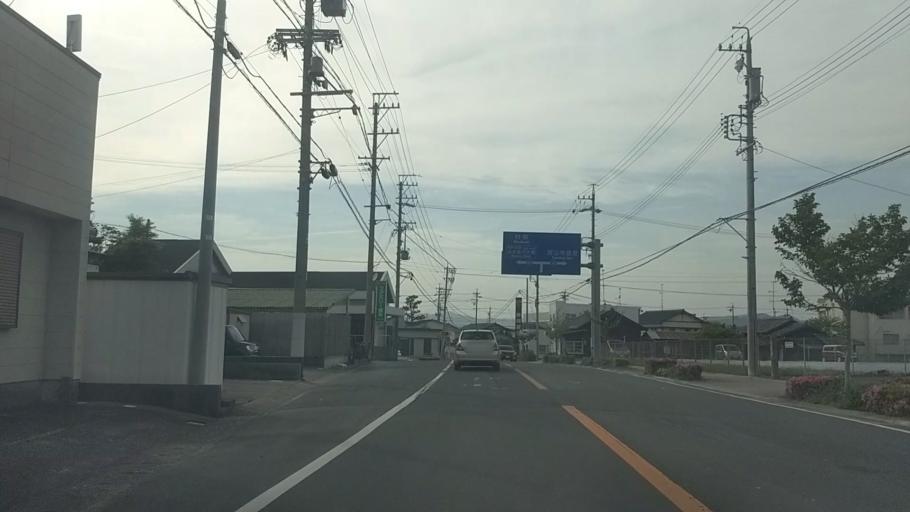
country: JP
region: Shizuoka
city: Kosai-shi
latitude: 34.7617
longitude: 137.6146
